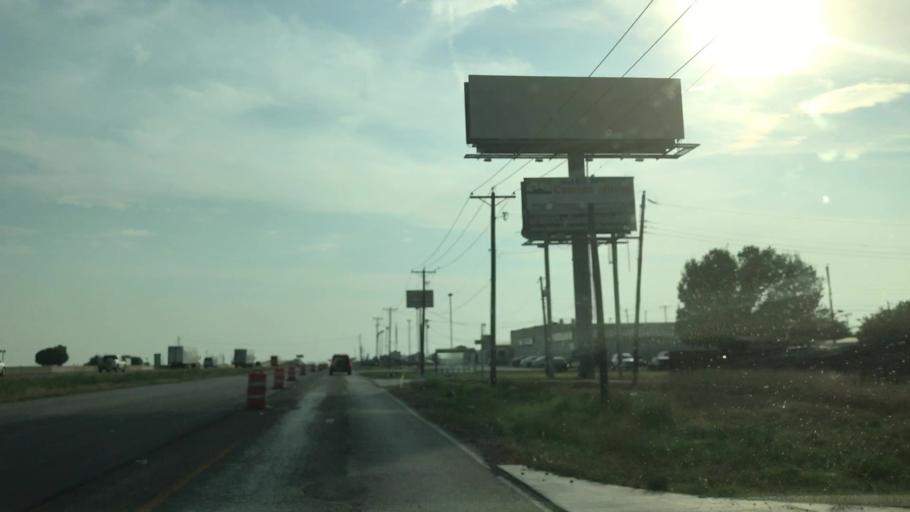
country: US
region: Texas
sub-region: Rockwall County
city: Fate
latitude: 32.9220
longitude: -96.4099
